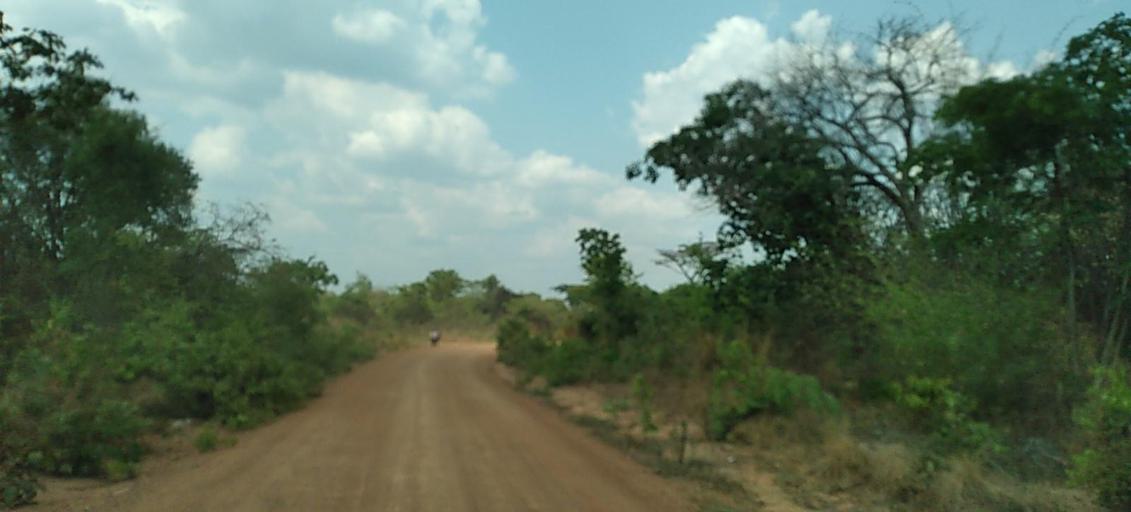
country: ZM
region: Copperbelt
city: Luanshya
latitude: -13.1421
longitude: 28.3284
